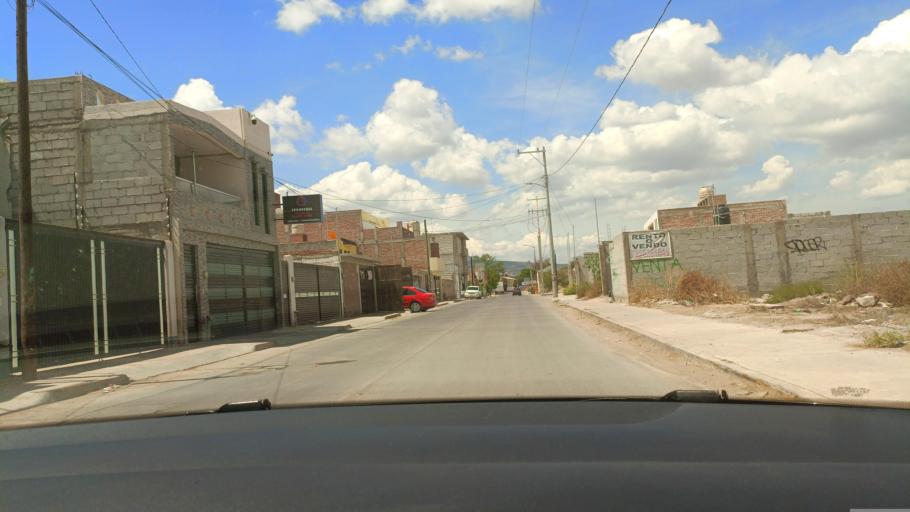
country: MX
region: Guanajuato
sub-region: San Luis de la Paz
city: San Luis de la Paz
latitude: 21.3048
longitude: -100.5213
